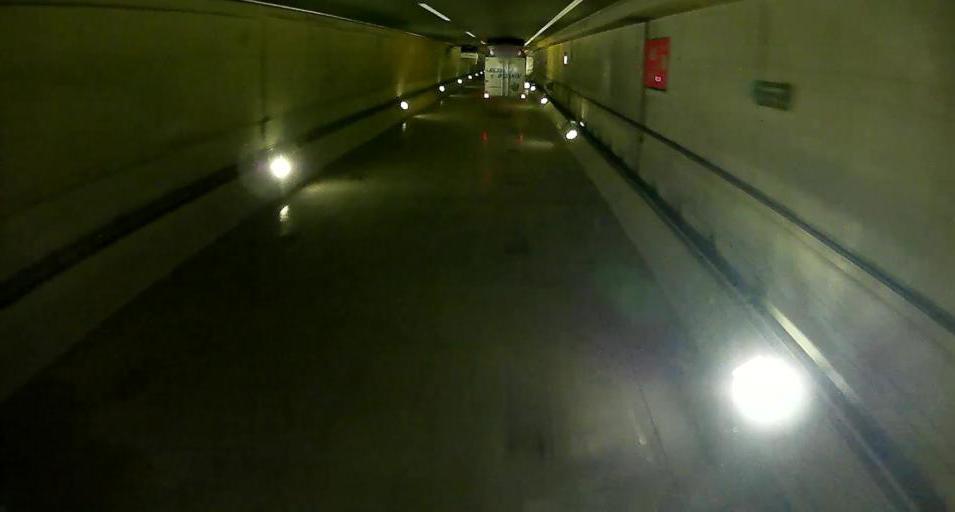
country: JP
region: Chiba
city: Chiba
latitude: 35.6096
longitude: 140.1068
